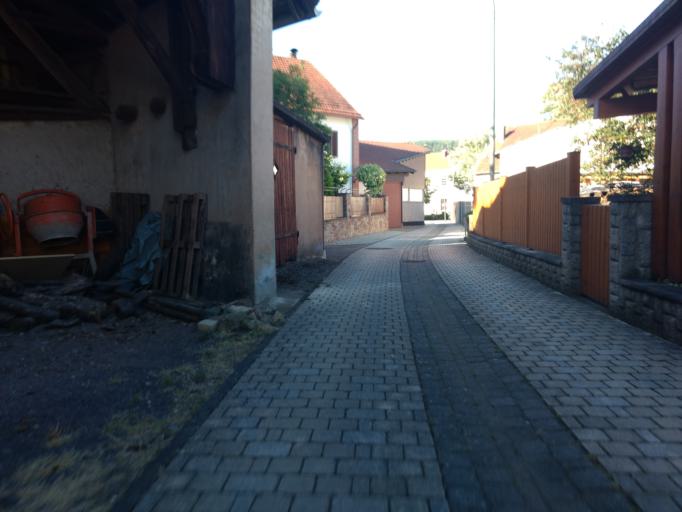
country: DE
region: Saarland
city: Merzig
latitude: 49.4187
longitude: 6.6308
